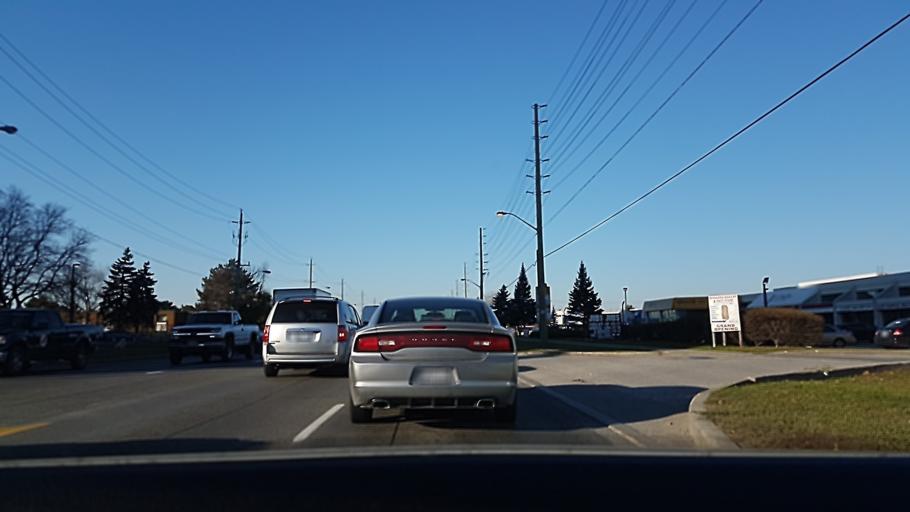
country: CA
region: Ontario
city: Concord
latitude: 43.7750
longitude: -79.5238
